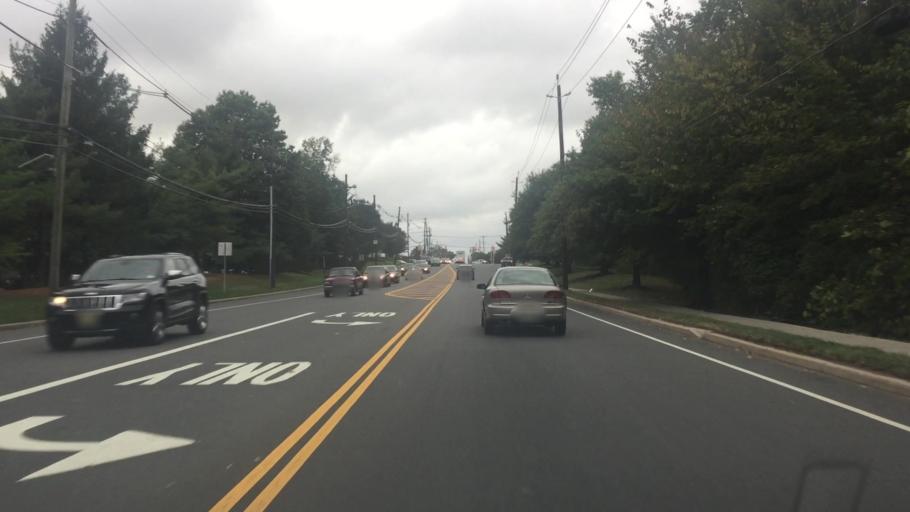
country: US
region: New Jersey
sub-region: Middlesex County
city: Edison
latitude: 40.5420
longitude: -74.3948
